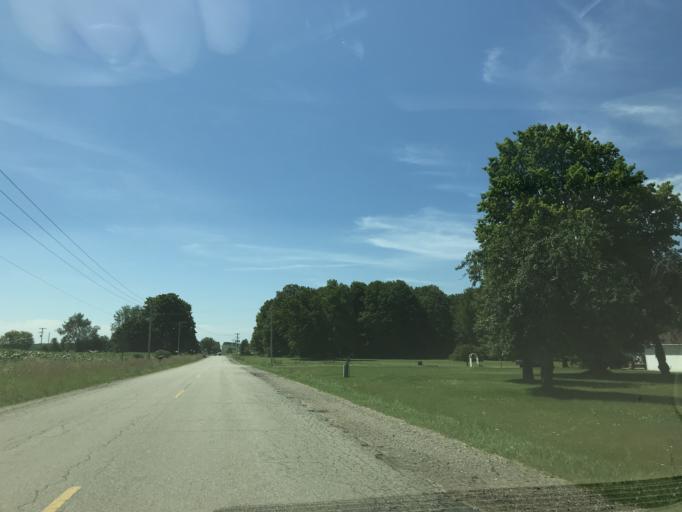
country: US
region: Michigan
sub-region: Missaukee County
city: Lake City
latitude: 44.3255
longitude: -85.0750
